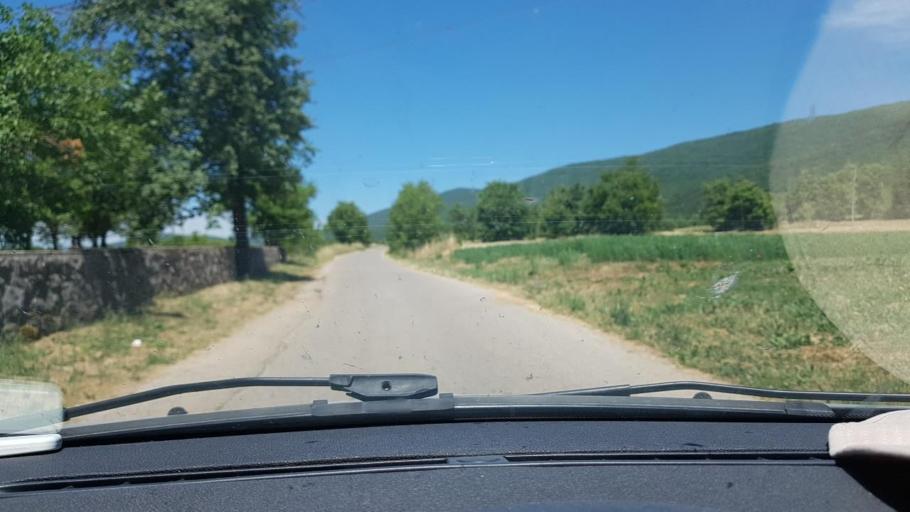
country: HR
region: Licko-Senjska
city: Otocac
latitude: 44.7949
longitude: 15.3653
